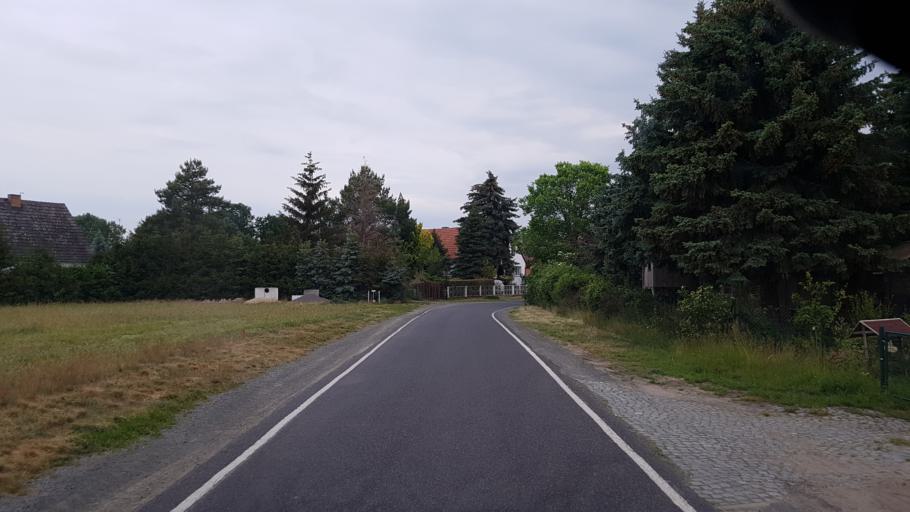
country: DE
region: Brandenburg
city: Herzberg
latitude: 51.7970
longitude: 13.2384
